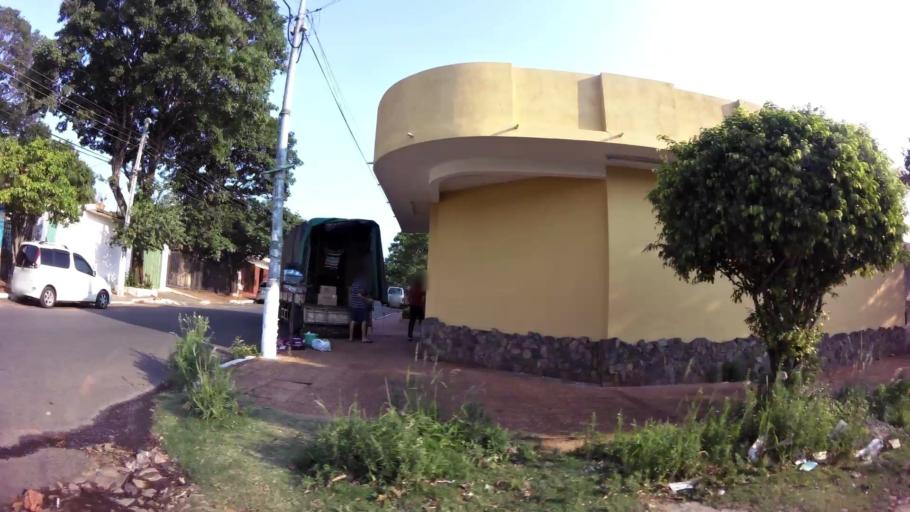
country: PY
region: Central
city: Lambare
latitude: -25.3436
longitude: -57.5998
